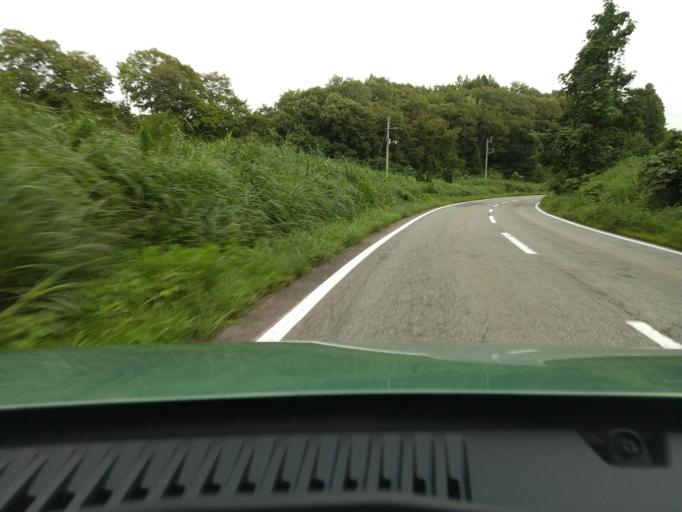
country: JP
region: Akita
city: Akita
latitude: 39.7280
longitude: 140.1834
